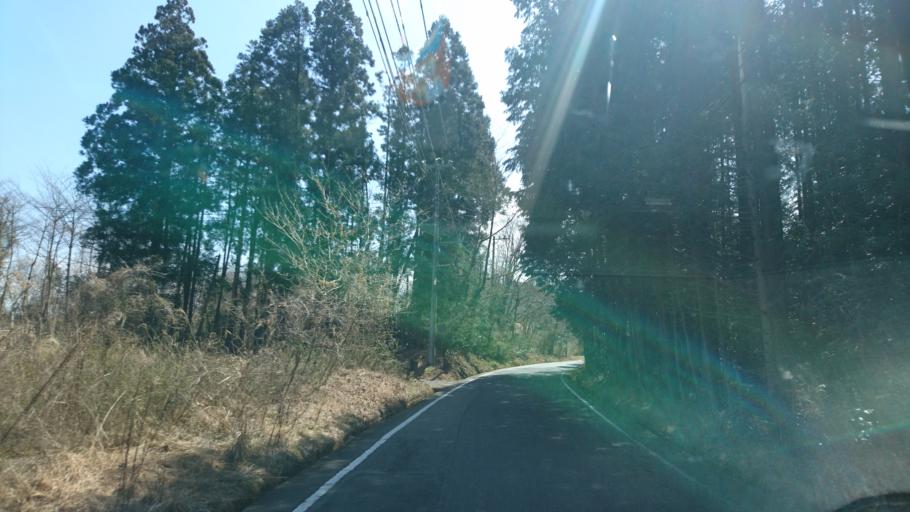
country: JP
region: Shizuoka
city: Fujinomiya
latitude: 35.3527
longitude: 138.5716
